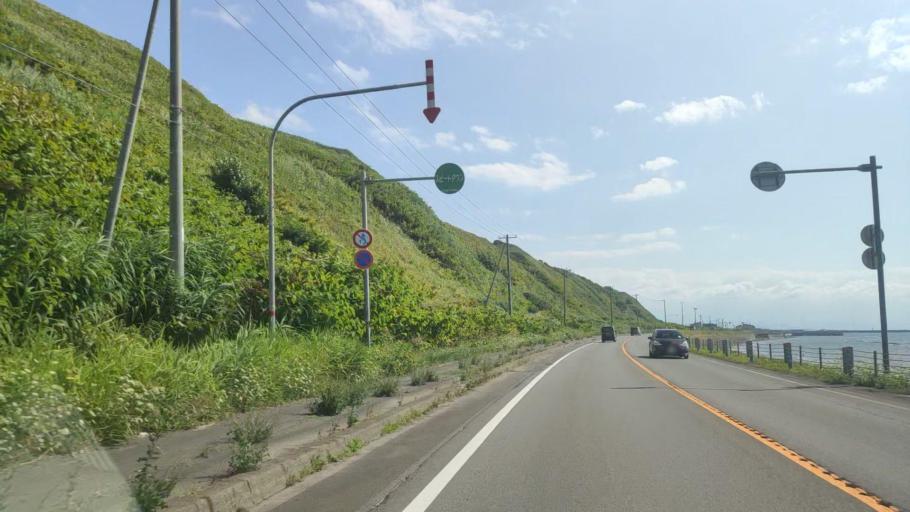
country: JP
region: Hokkaido
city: Rumoi
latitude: 43.9900
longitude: 141.6509
